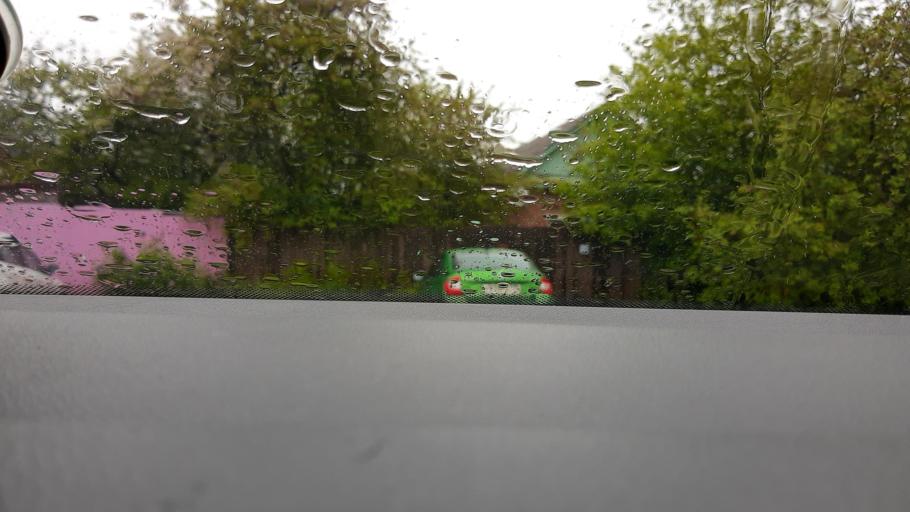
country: RU
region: Moskovskaya
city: Shcherbinka
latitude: 55.5035
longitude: 37.5528
